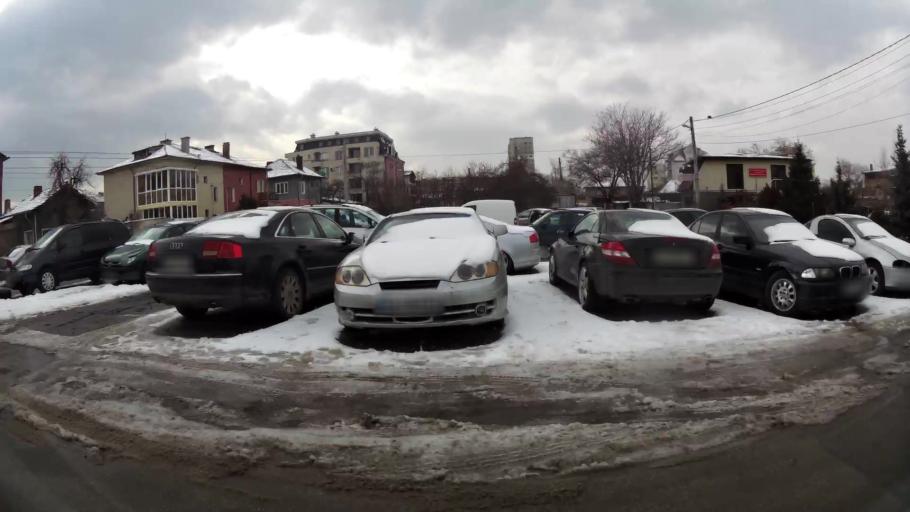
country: BG
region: Sofia-Capital
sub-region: Stolichna Obshtina
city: Sofia
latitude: 42.7075
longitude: 23.3729
